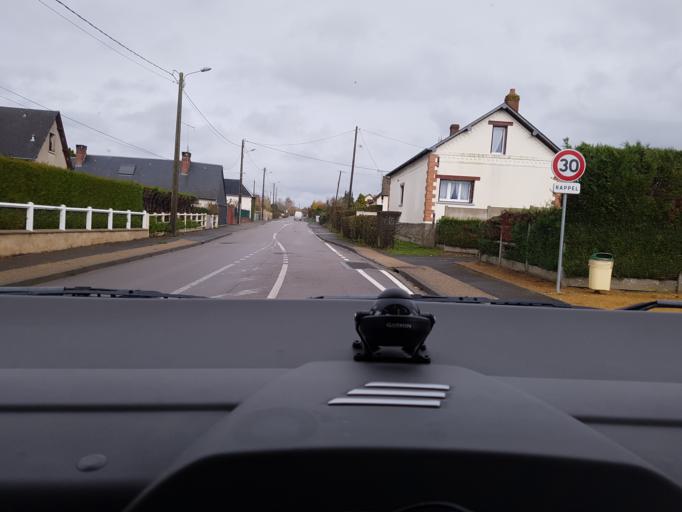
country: FR
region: Haute-Normandie
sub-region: Departement de la Seine-Maritime
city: Gournay-en-Bray
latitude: 49.4849
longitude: 1.7422
